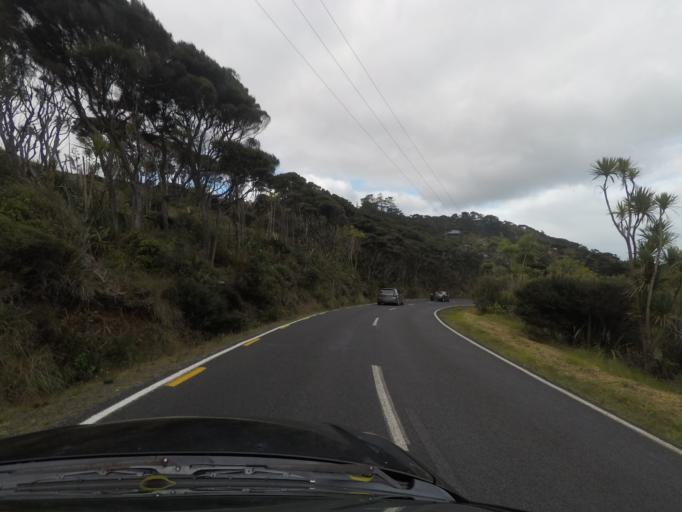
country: NZ
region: Auckland
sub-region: Auckland
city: Muriwai Beach
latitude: -36.8777
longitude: 174.4521
